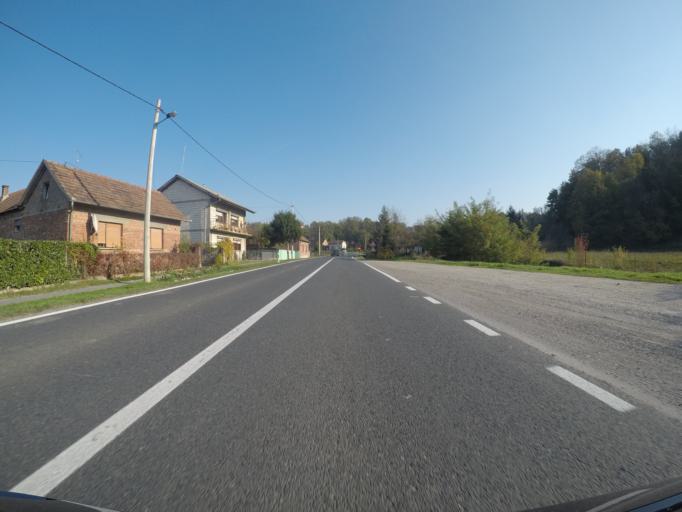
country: HR
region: Koprivnicko-Krizevacka
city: Virje
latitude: 46.0234
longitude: 16.9848
